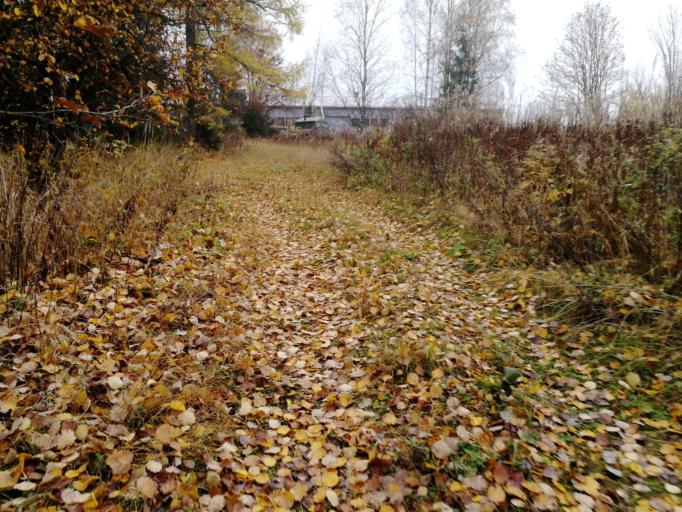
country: FI
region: Pirkanmaa
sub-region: Tampere
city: Tampere
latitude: 61.4495
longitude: 23.8989
